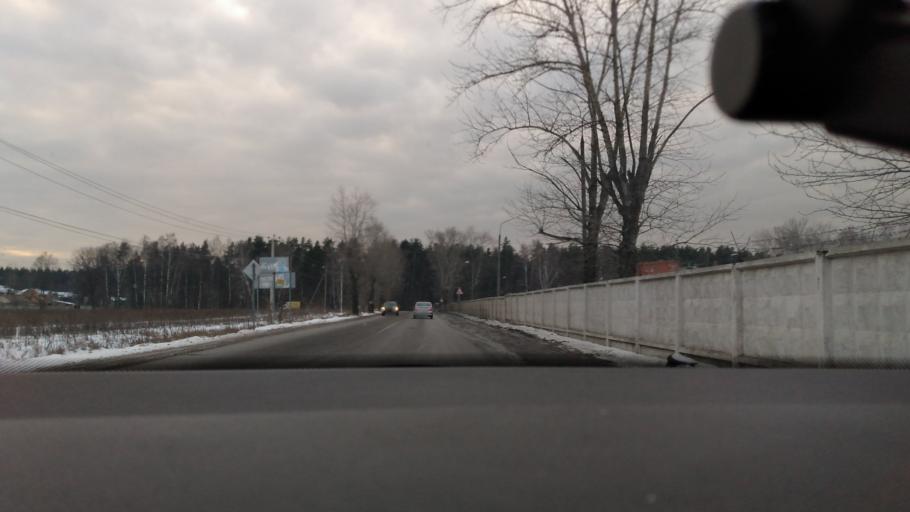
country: RU
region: Moskovskaya
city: Rodniki
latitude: 55.6781
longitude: 38.1105
